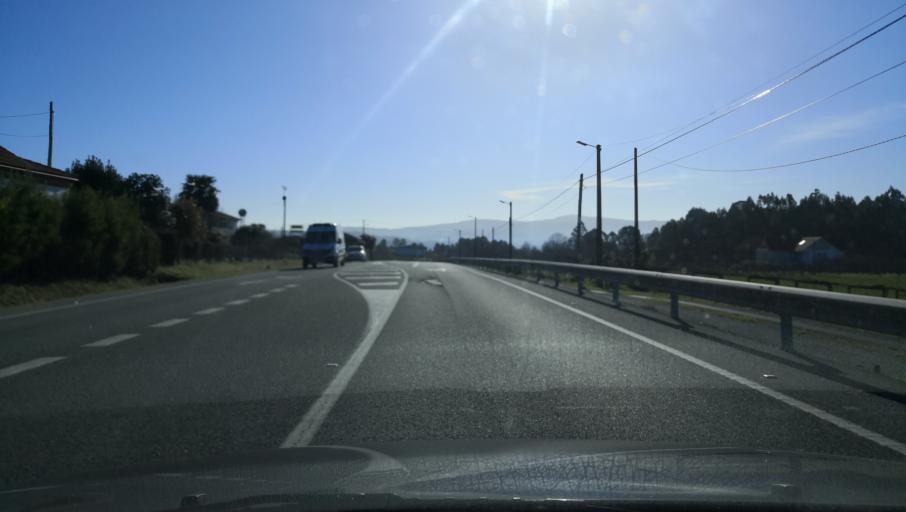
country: ES
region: Galicia
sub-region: Provincia da Coruna
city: Vedra
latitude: 42.7854
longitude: -8.4393
